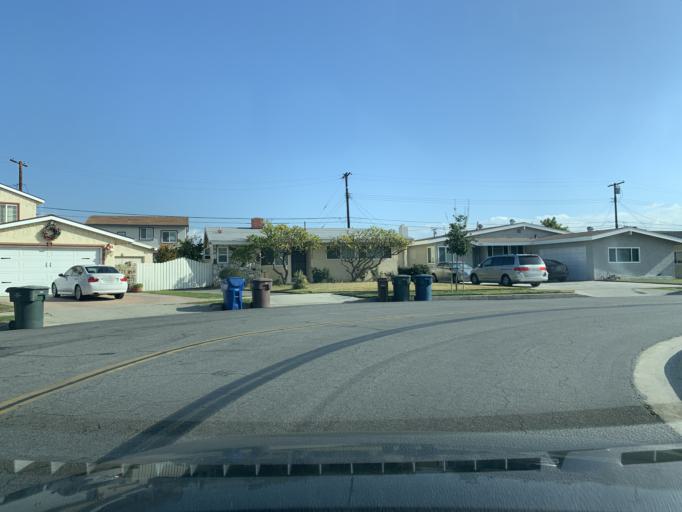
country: US
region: California
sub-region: Los Angeles County
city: South El Monte
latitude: 34.0684
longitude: -118.0536
